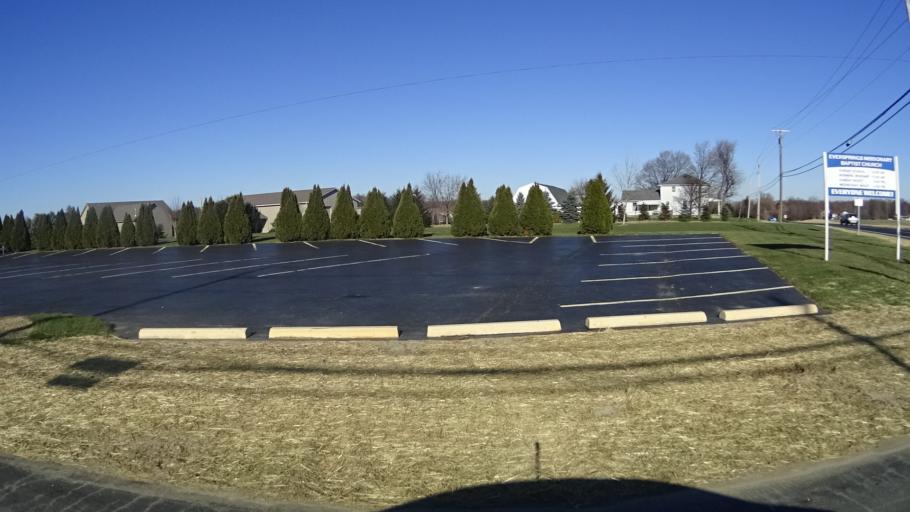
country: US
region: Ohio
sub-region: Lorain County
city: South Amherst
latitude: 41.3758
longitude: -82.2822
